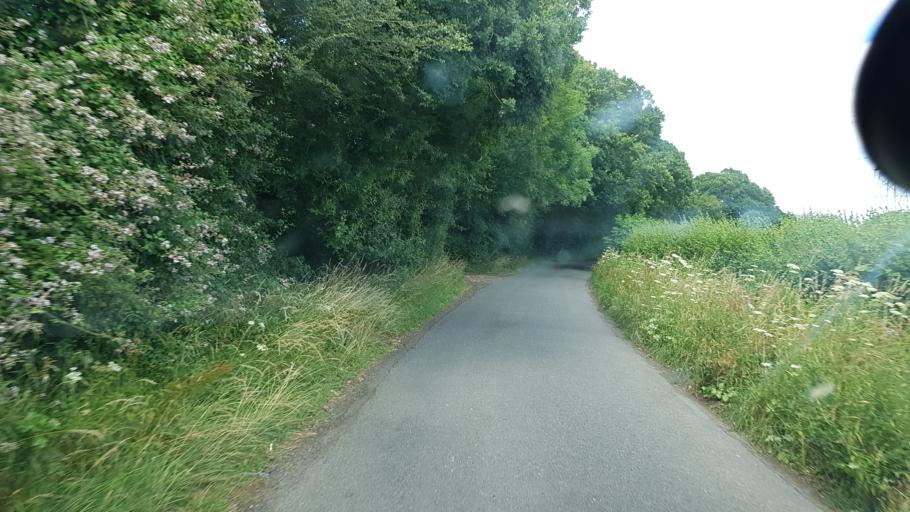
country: GB
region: England
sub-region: West Sussex
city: Billingshurst
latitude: 51.0234
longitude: -0.4359
